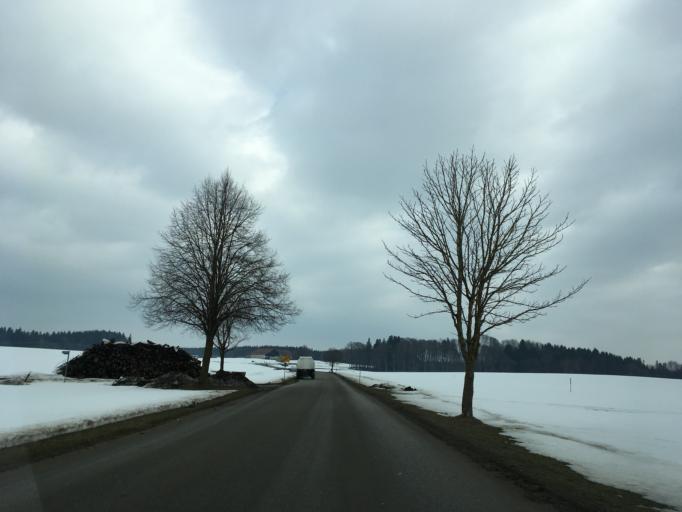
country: DE
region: Bavaria
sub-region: Upper Bavaria
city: Bad Endorf
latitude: 47.9063
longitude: 12.3150
